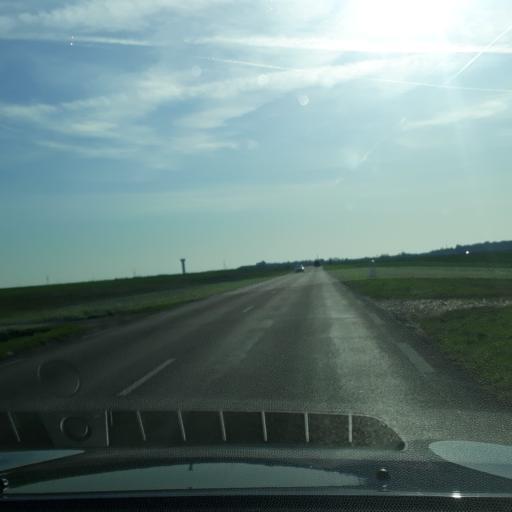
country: FR
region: Ile-de-France
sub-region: Departement de l'Essonne
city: Corbreuse
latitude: 48.4490
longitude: 1.9779
